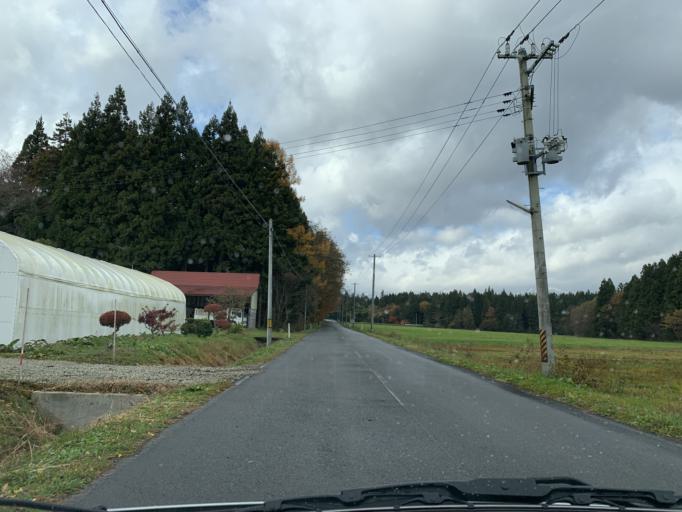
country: JP
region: Iwate
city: Mizusawa
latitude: 39.1034
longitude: 140.9912
